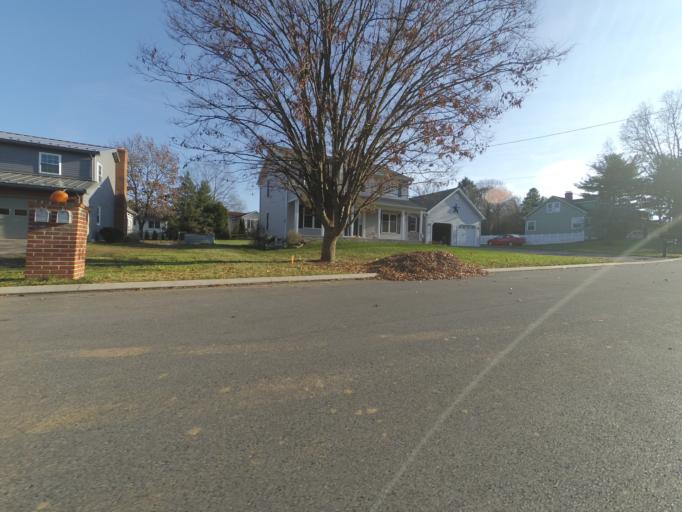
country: US
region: Pennsylvania
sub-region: Centre County
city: Lemont
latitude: 40.7998
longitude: -77.8290
